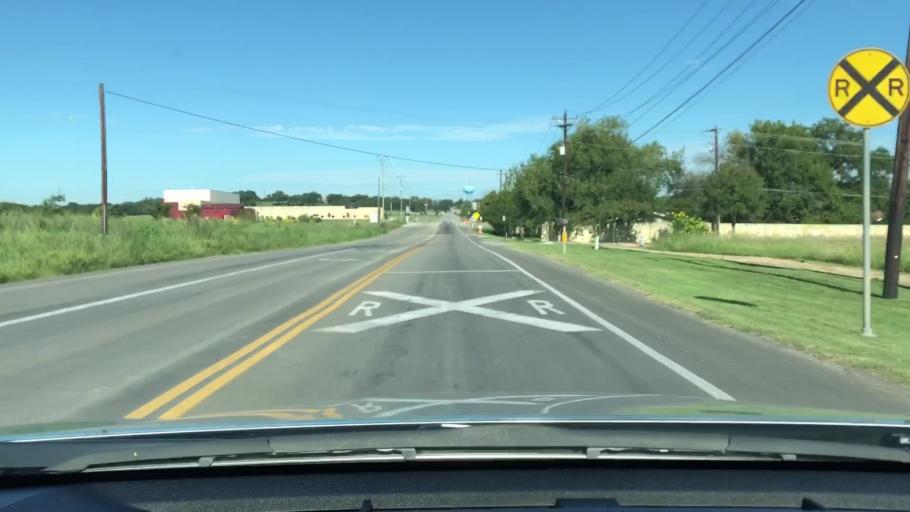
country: US
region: Texas
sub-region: Hays County
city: San Marcos
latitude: 29.8421
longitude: -97.9749
